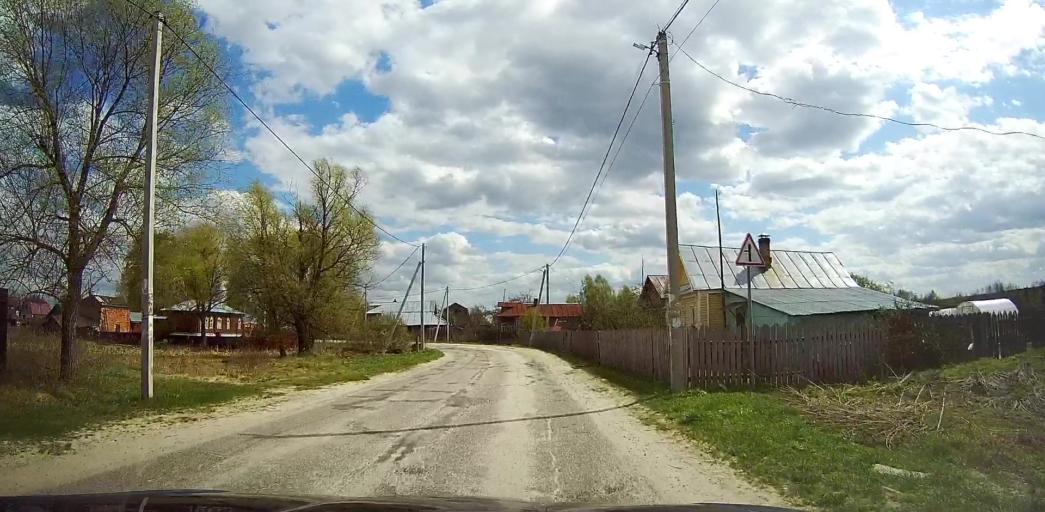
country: RU
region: Moskovskaya
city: Davydovo
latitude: 55.6391
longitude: 38.7777
